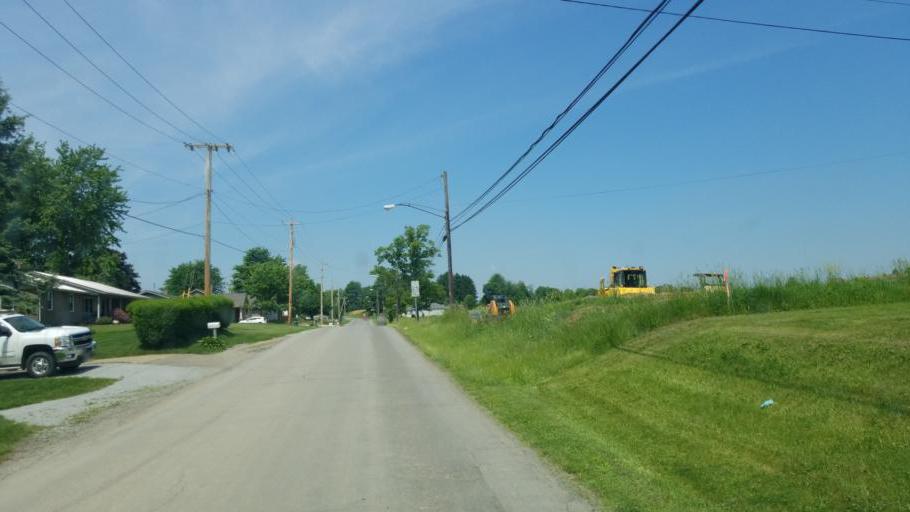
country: US
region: Ohio
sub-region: Tuscarawas County
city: Sugarcreek
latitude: 40.5134
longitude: -81.6605
